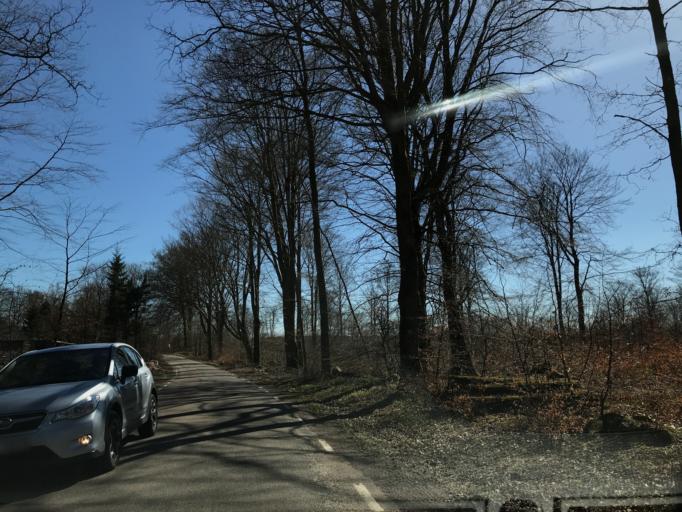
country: SE
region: Skane
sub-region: Svalovs Kommun
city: Kagerod
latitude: 56.0294
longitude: 13.1581
